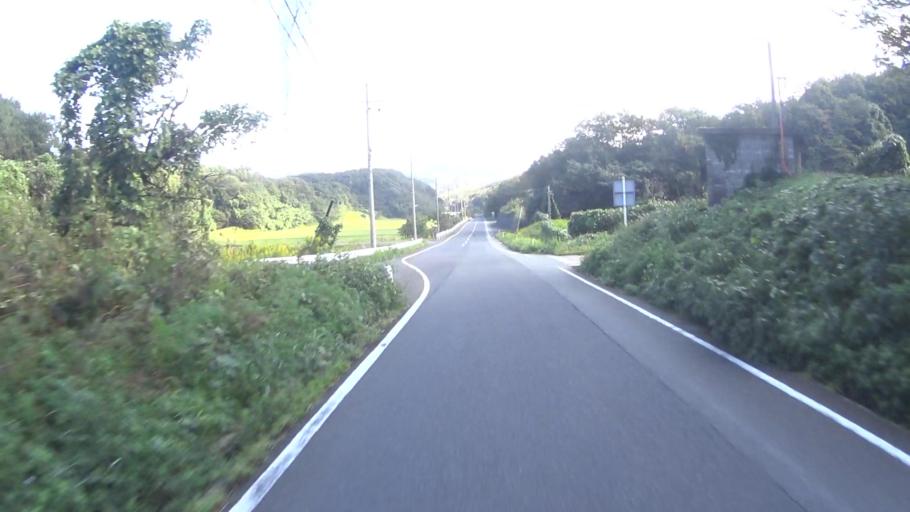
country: JP
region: Kyoto
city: Miyazu
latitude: 35.7018
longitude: 135.0701
